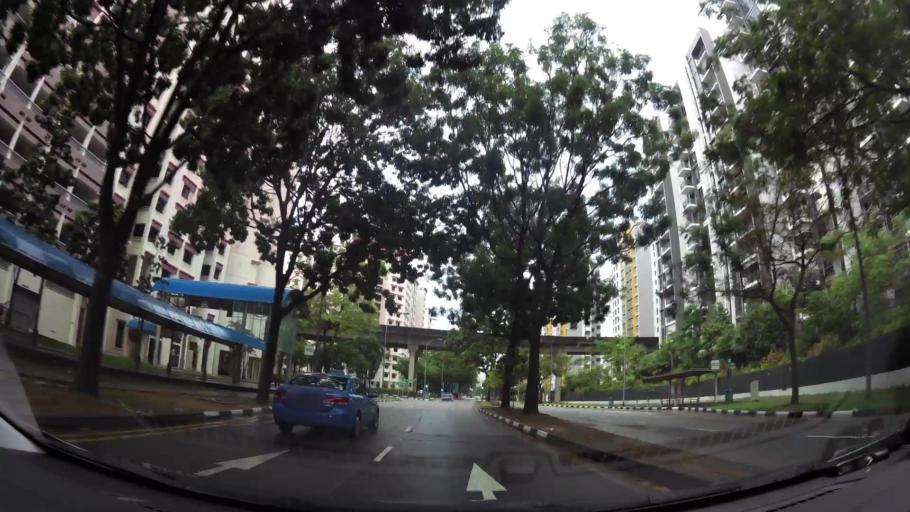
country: MY
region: Johor
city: Kampung Pasir Gudang Baru
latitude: 1.3885
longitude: 103.8952
